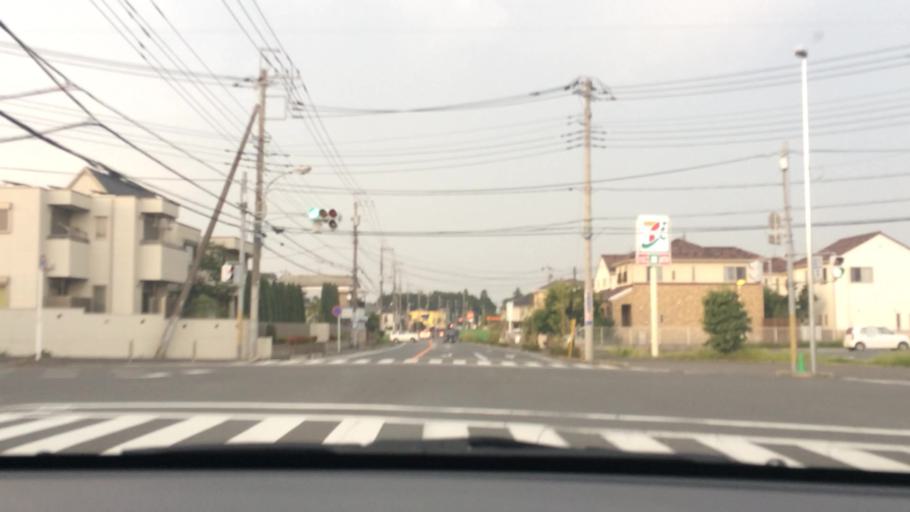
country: JP
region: Chiba
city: Nagareyama
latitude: 35.8760
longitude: 139.9172
